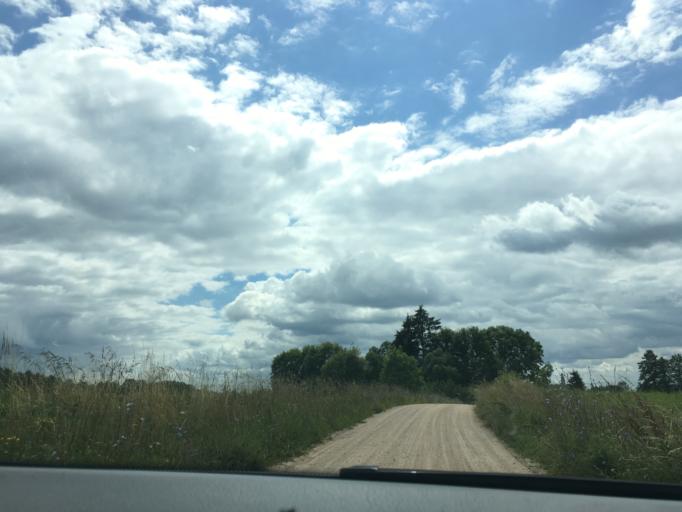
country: PL
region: Podlasie
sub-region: Powiat sejnenski
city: Krasnopol
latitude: 54.0954
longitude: 23.2712
